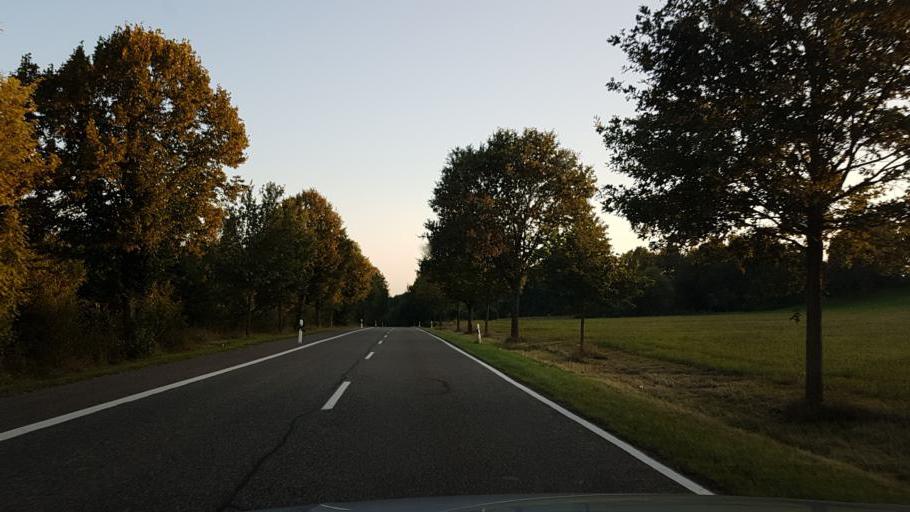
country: DE
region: Saarland
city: Weiskirchen
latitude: 49.5314
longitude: 6.8324
